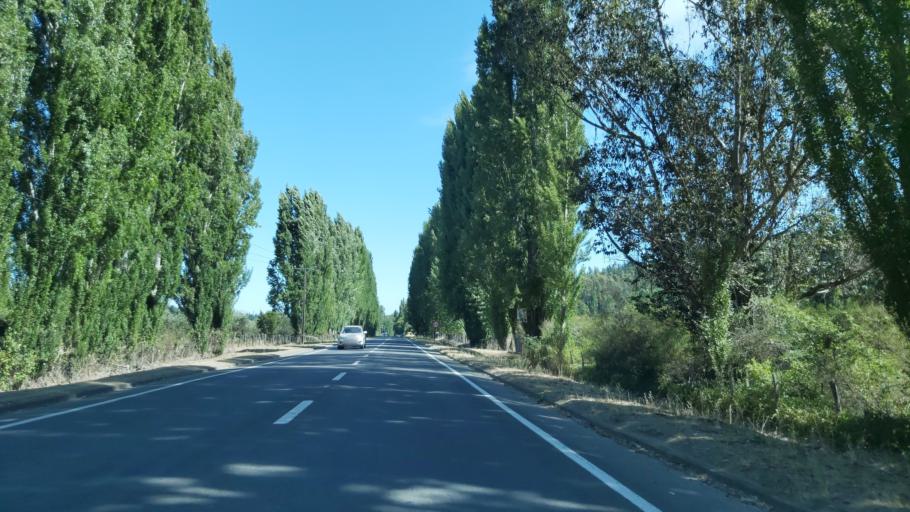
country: CL
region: Biobio
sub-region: Provincia de Concepcion
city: Lota
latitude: -37.1448
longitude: -72.9780
